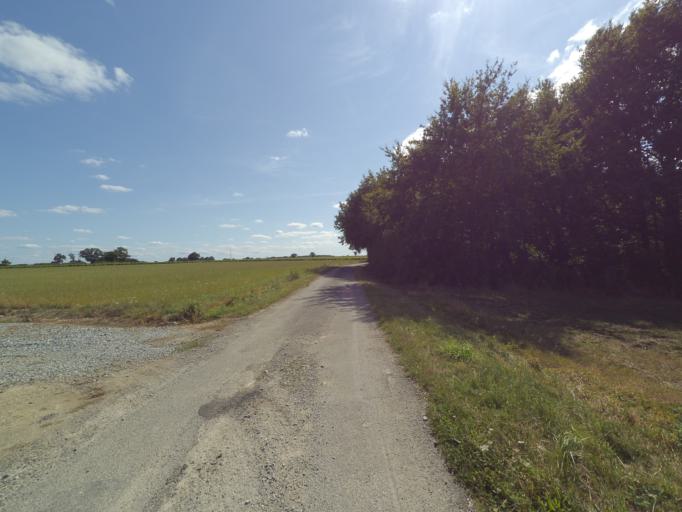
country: FR
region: Pays de la Loire
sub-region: Departement de la Loire-Atlantique
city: Vieillevigne
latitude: 46.9632
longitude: -1.4437
